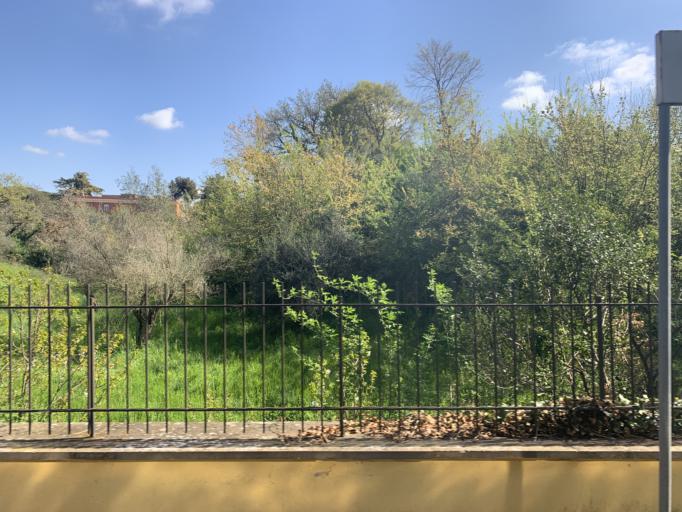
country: IT
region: Latium
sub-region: Citta metropolitana di Roma Capitale
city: Marino
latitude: 41.7790
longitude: 12.6353
